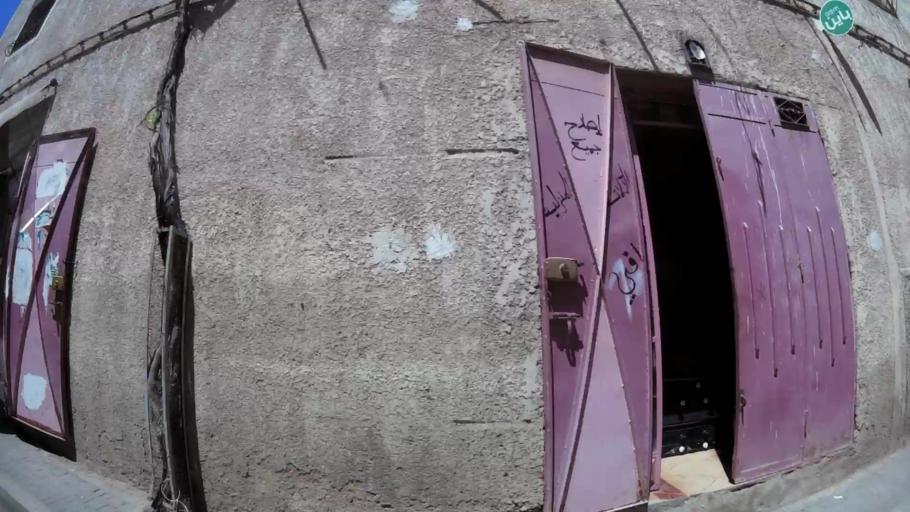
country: MA
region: Oriental
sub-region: Oujda-Angad
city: Oujda
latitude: 34.6823
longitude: -1.9548
